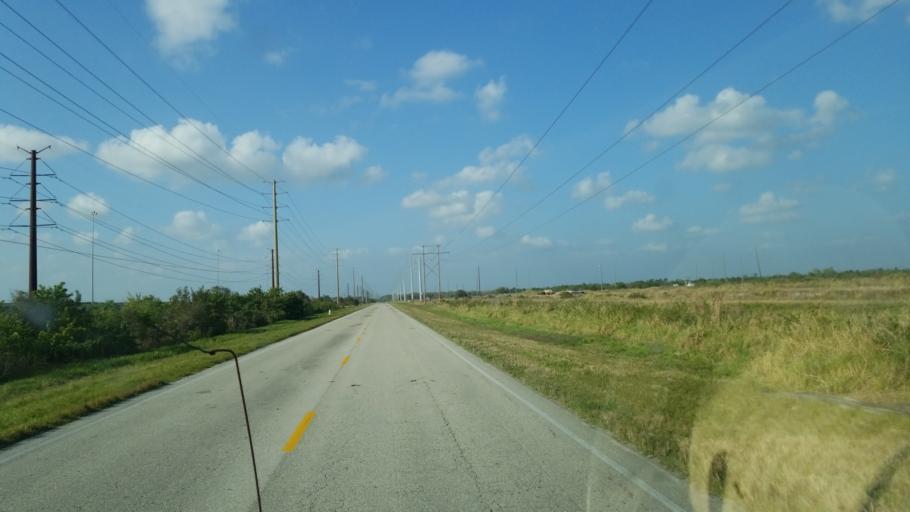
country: US
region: Florida
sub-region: Hardee County
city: Wauchula
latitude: 27.5688
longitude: -81.9348
